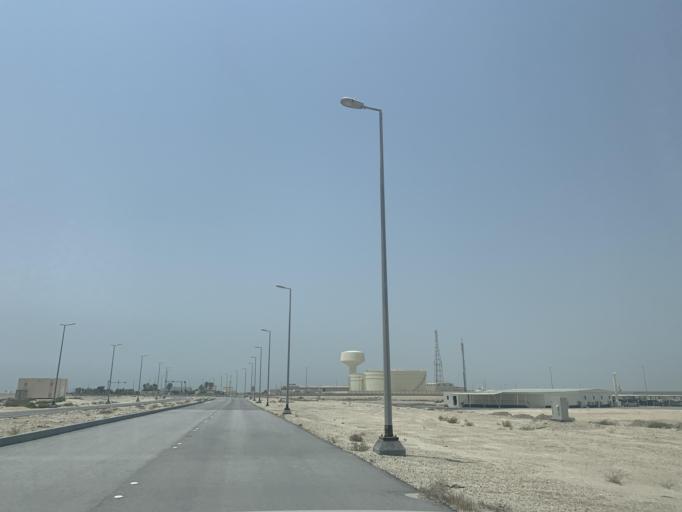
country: BH
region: Central Governorate
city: Dar Kulayb
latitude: 25.8422
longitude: 50.5885
